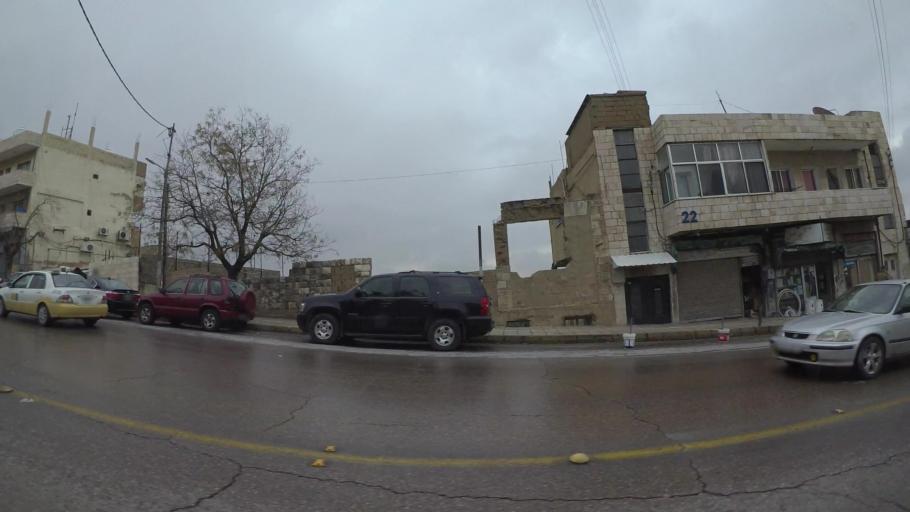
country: JO
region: Amman
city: Amman
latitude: 31.9588
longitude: 35.9322
